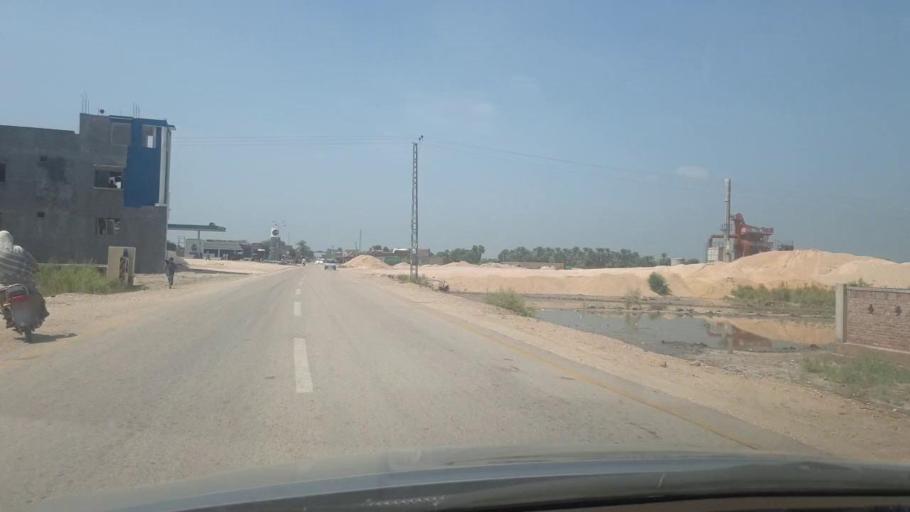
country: PK
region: Sindh
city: Bozdar
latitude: 27.2264
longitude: 68.5673
